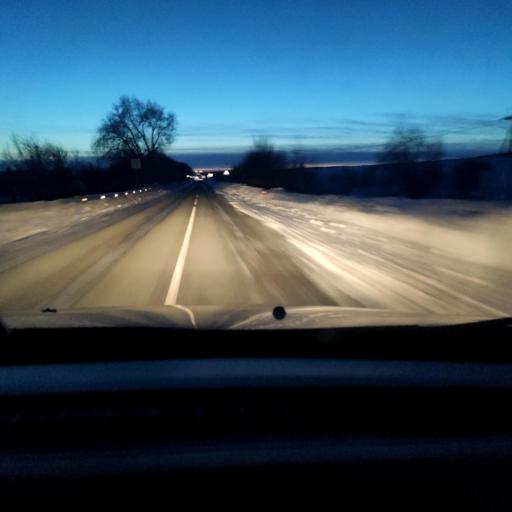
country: RU
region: Samara
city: Kinel'
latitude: 53.2852
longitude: 50.6634
